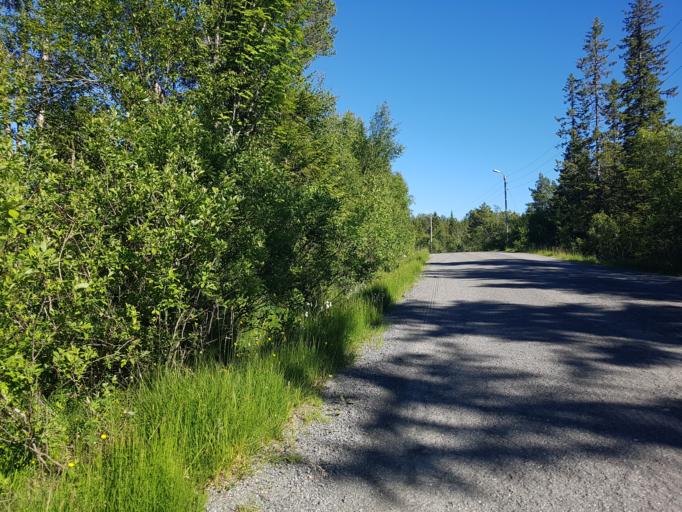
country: NO
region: Sor-Trondelag
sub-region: Trondheim
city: Trondheim
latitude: 63.4288
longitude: 10.2803
